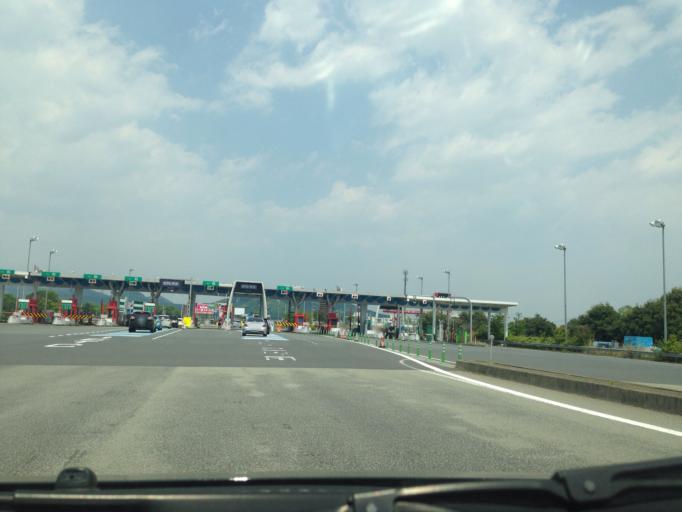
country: JP
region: Tochigi
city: Utsunomiya-shi
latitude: 36.6329
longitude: 139.8447
